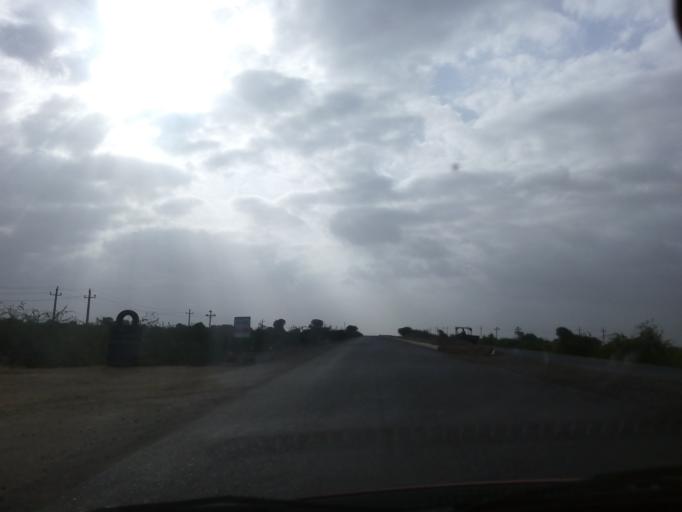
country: IN
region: Gujarat
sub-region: Kachchh
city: Bhachau
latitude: 23.3336
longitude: 70.2076
